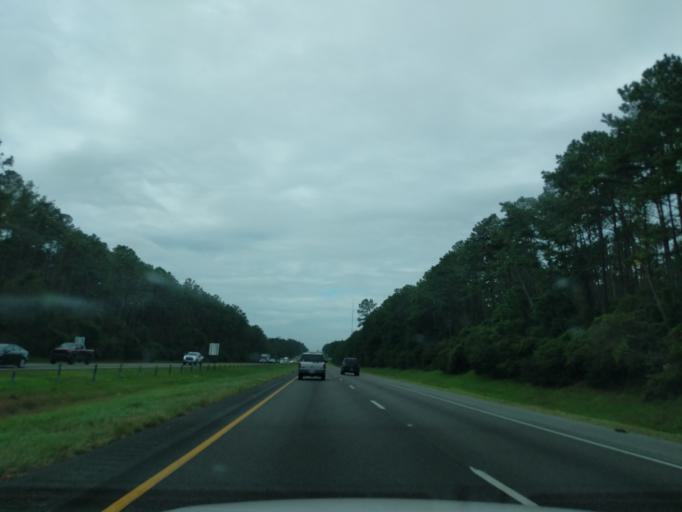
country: US
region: Alabama
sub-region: Baldwin County
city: Spanish Fort
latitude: 30.6613
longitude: -87.8733
